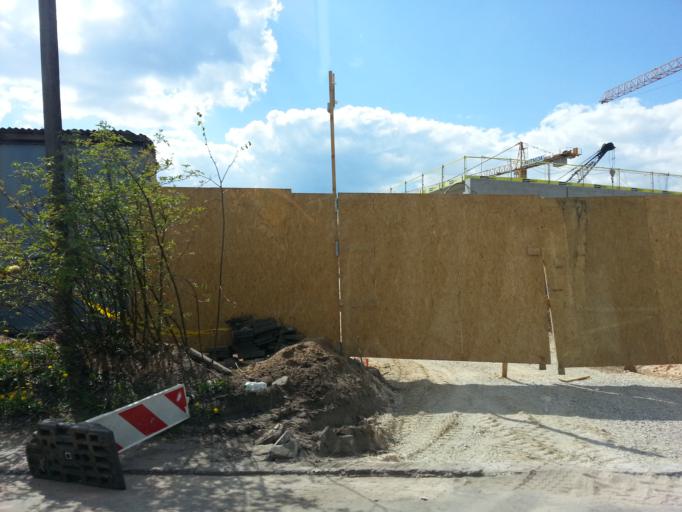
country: LT
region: Vilnius County
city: Vilkpede
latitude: 54.6691
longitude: 25.2606
